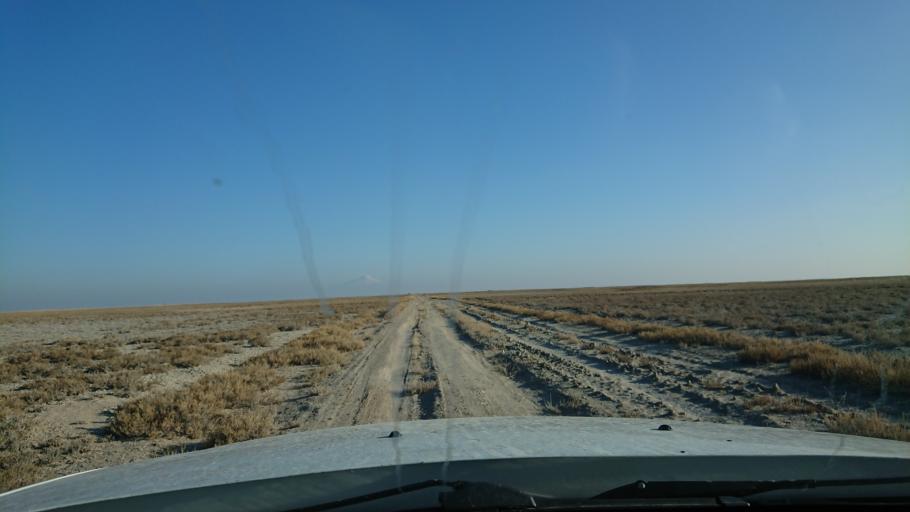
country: TR
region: Aksaray
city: Eskil
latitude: 38.4070
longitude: 33.5696
